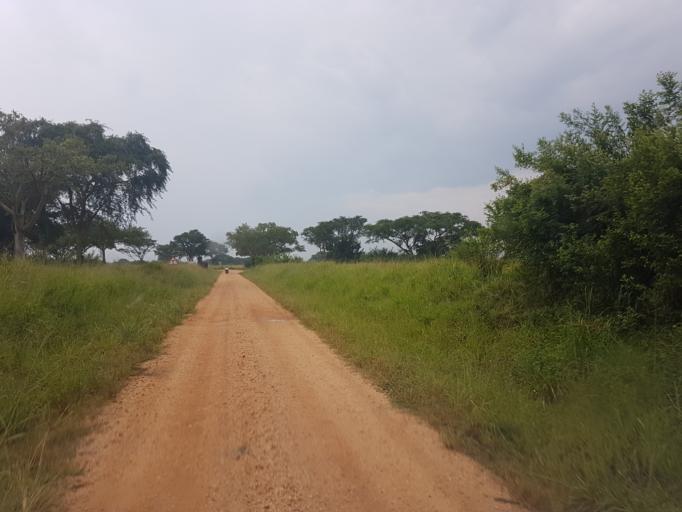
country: UG
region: Western Region
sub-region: Mitoma District
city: Mitoma
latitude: -0.4931
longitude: 29.8005
